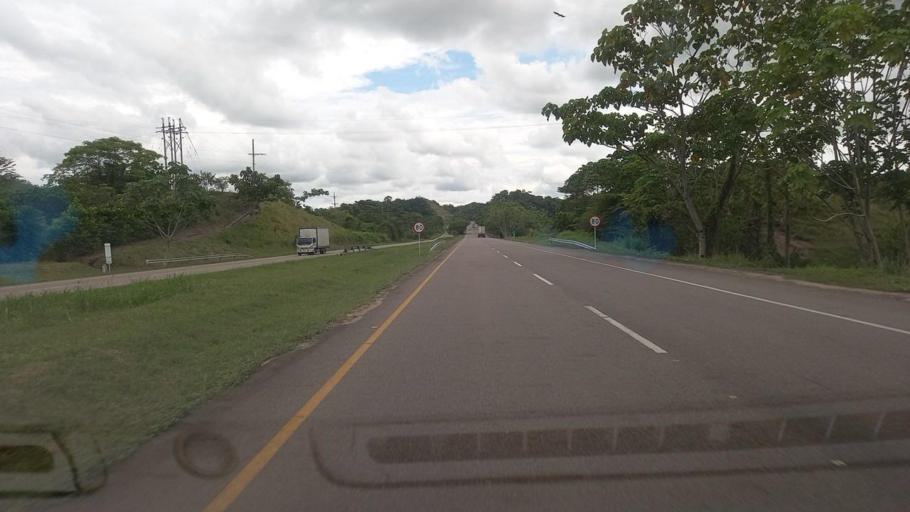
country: CO
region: Boyaca
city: Puerto Boyaca
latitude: 6.1433
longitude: -74.5579
